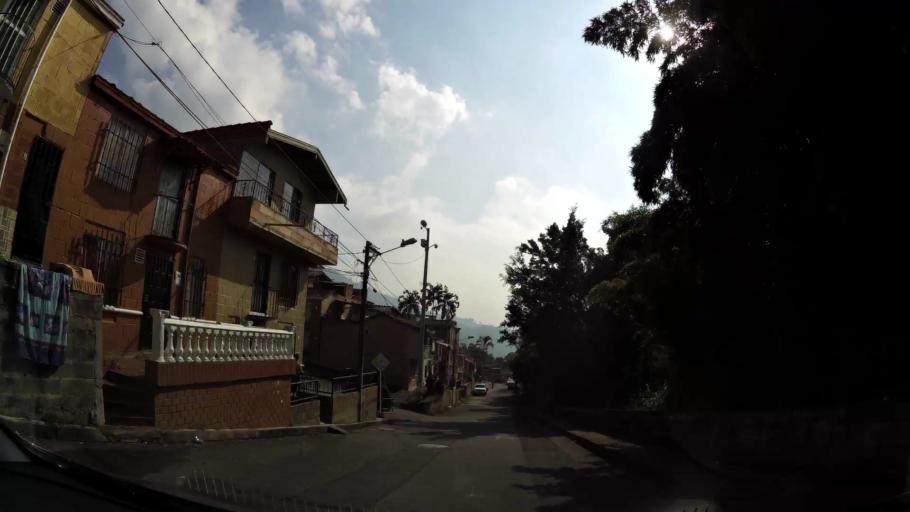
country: CO
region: Antioquia
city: La Estrella
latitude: 6.1713
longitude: -75.6376
